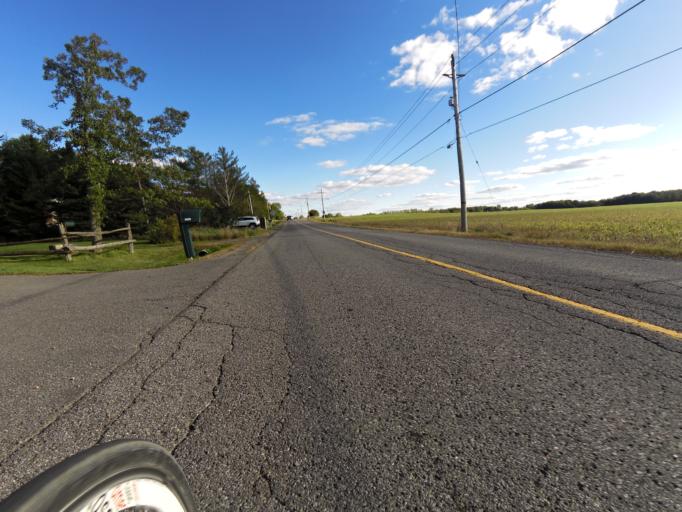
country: CA
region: Ontario
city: Bells Corners
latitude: 45.1210
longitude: -75.7372
